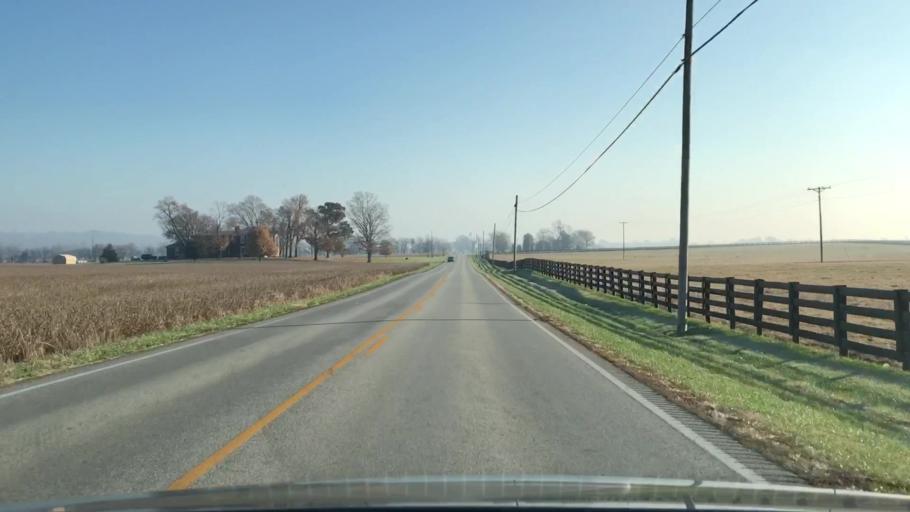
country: US
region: Kentucky
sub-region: Edmonson County
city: Brownsville
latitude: 37.0642
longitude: -86.2836
